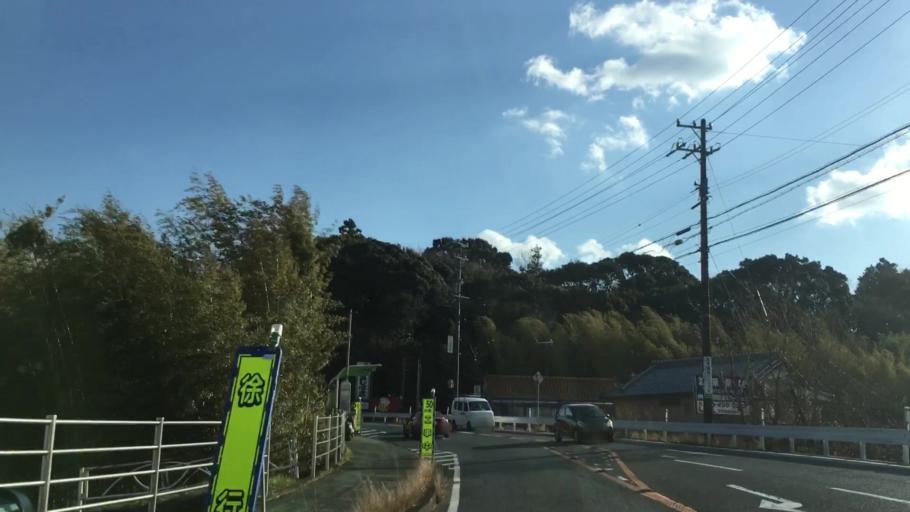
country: JP
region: Shizuoka
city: Hamamatsu
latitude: 34.7472
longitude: 137.6731
